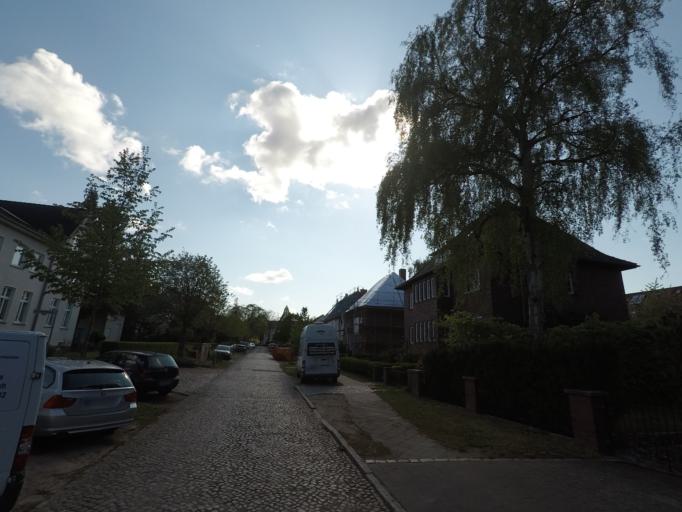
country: DE
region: Mecklenburg-Vorpommern
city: Rostock
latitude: 54.0805
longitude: 12.1055
